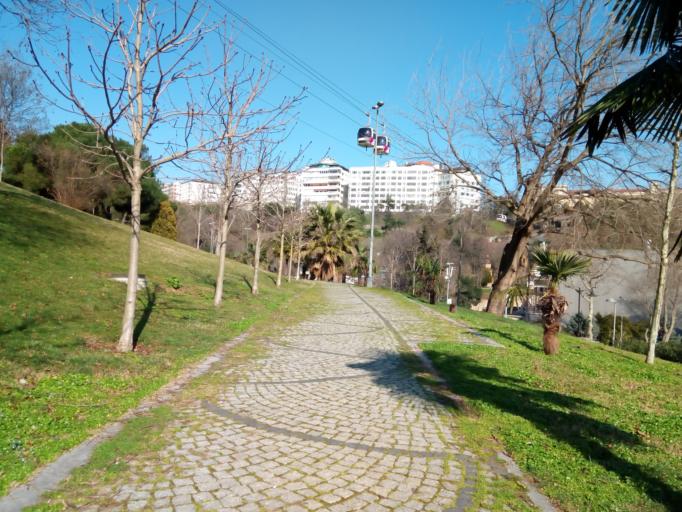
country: TR
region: Istanbul
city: Sisli
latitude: 41.0436
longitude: 28.9913
